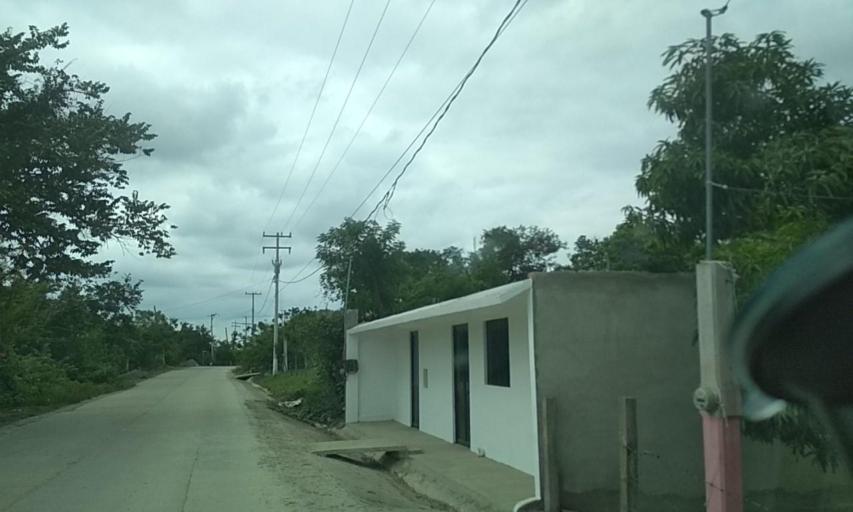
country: MX
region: Veracruz
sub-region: Papantla
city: Polutla
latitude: 20.5420
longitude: -97.2554
